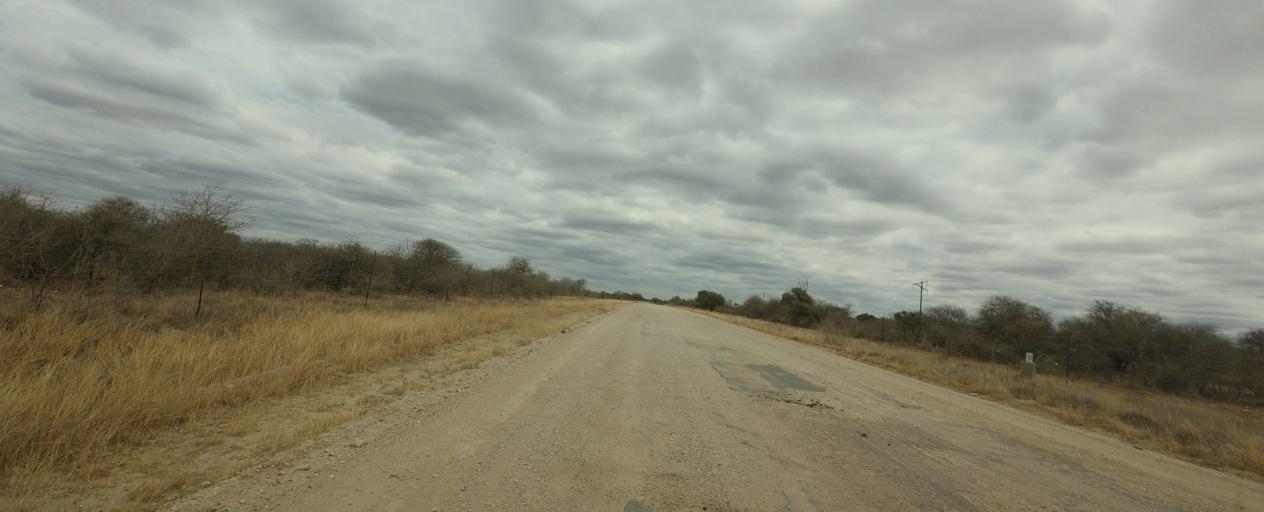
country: BW
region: Central
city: Mathathane
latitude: -22.7069
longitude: 28.5916
